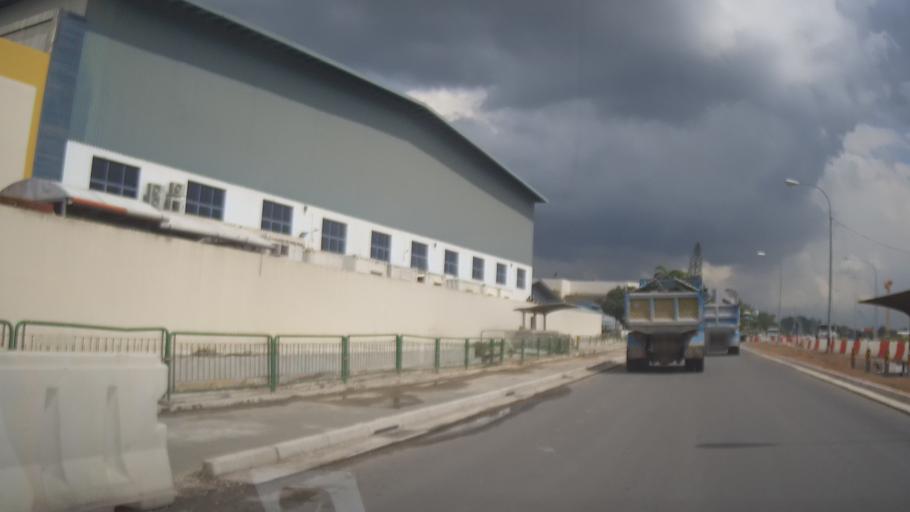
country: MY
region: Johor
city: Johor Bahru
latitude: 1.4346
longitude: 103.7510
